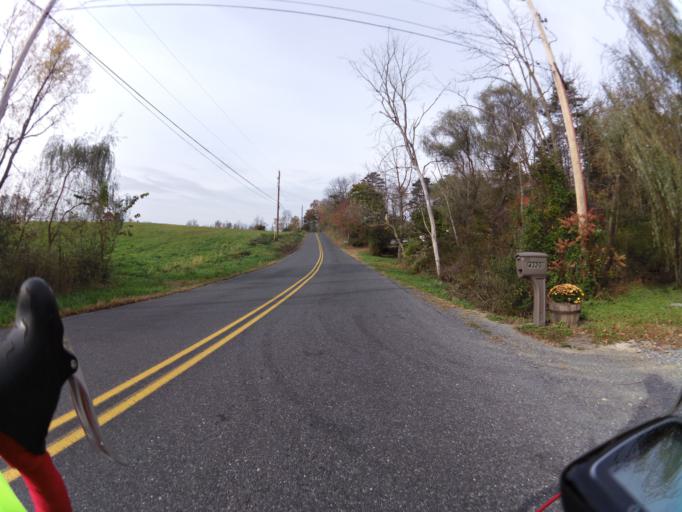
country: US
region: Pennsylvania
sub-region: Union County
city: New Columbia
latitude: 41.0511
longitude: -76.9313
